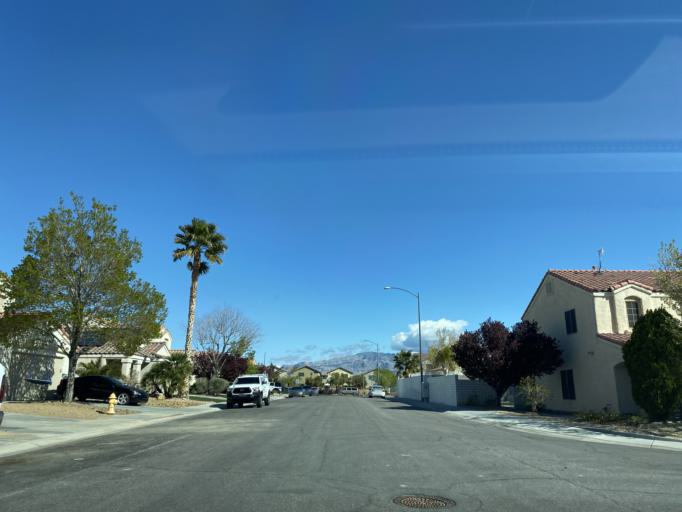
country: US
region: Nevada
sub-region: Clark County
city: Summerlin South
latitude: 36.3052
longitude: -115.2826
